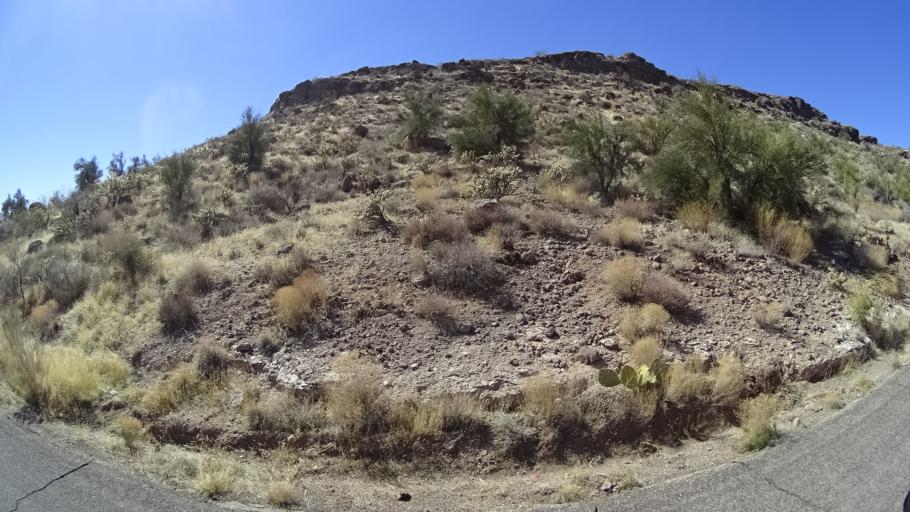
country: US
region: Arizona
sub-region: Mohave County
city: Kingman
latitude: 35.2007
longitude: -114.0602
